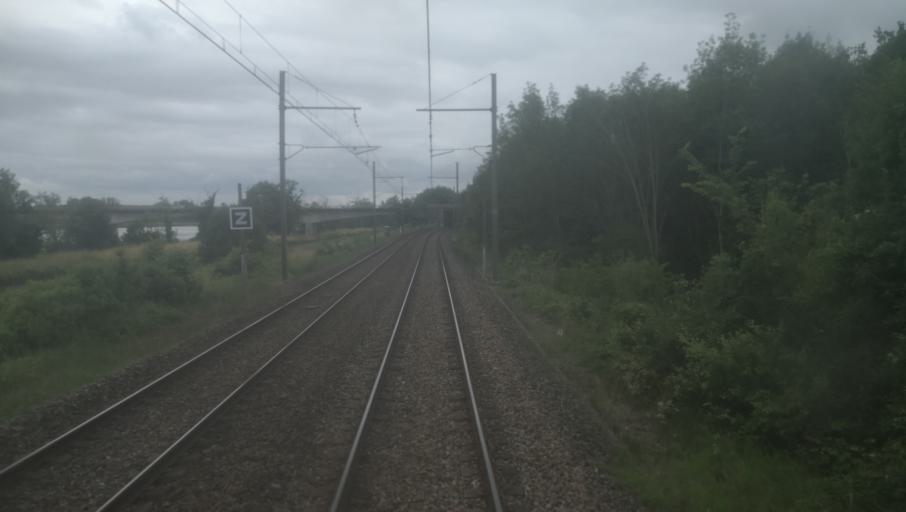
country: FR
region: Midi-Pyrenees
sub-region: Departement du Tarn-et-Garonne
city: Saint-Nicolas-de-la-Grave
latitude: 44.0869
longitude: 0.9876
